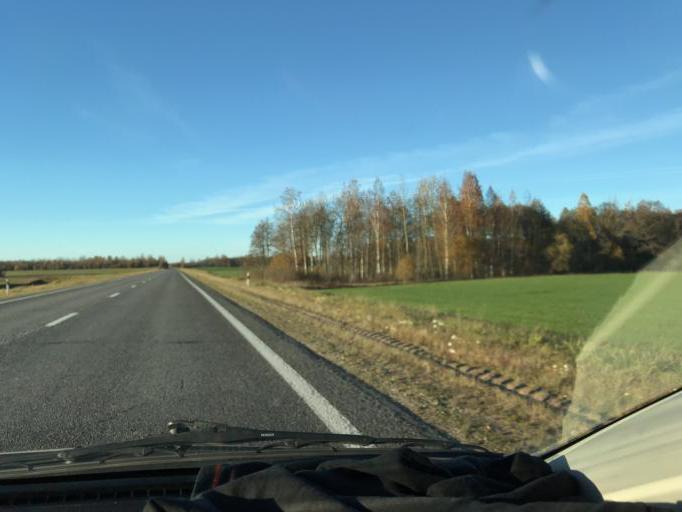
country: BY
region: Vitebsk
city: Haradok
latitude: 55.4134
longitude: 30.1089
